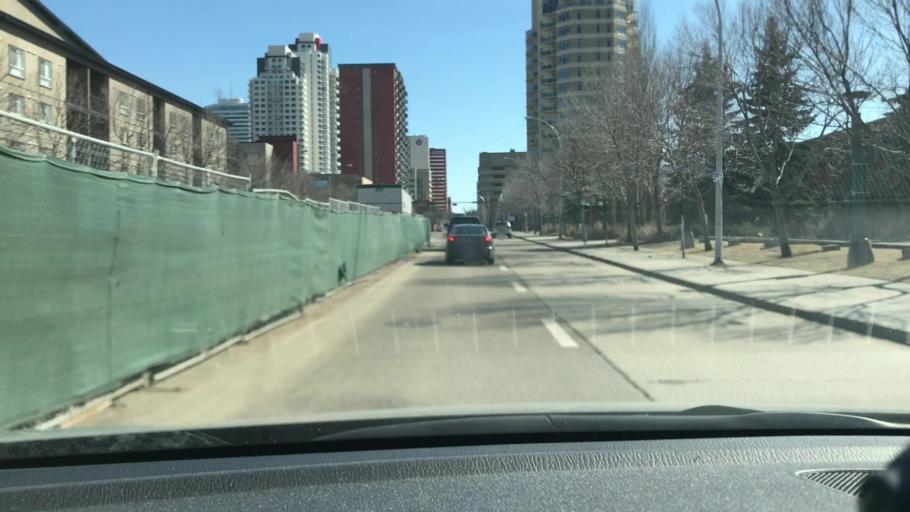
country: CA
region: Alberta
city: Edmonton
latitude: 53.5476
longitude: -113.5012
